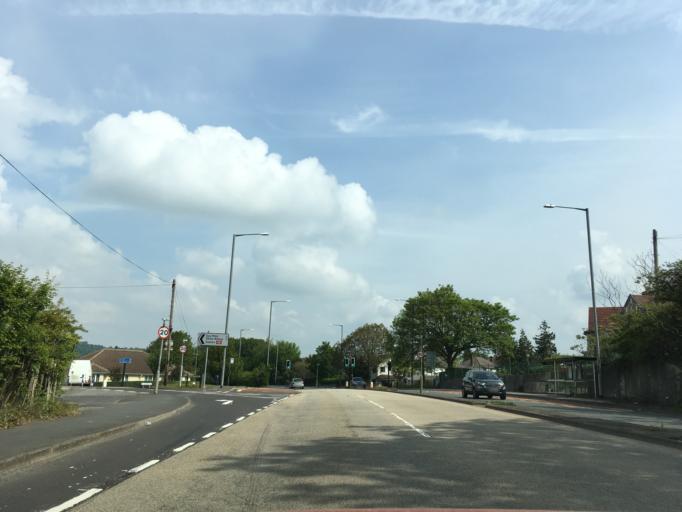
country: GB
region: England
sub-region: North Somerset
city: Long Ashton
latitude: 51.4783
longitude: -2.6481
